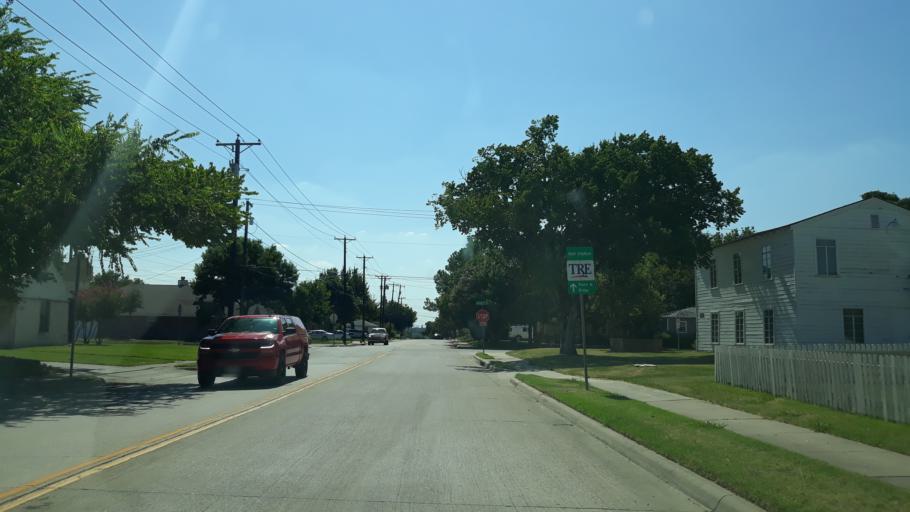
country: US
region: Texas
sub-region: Dallas County
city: Irving
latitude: 32.8173
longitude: -97.0018
